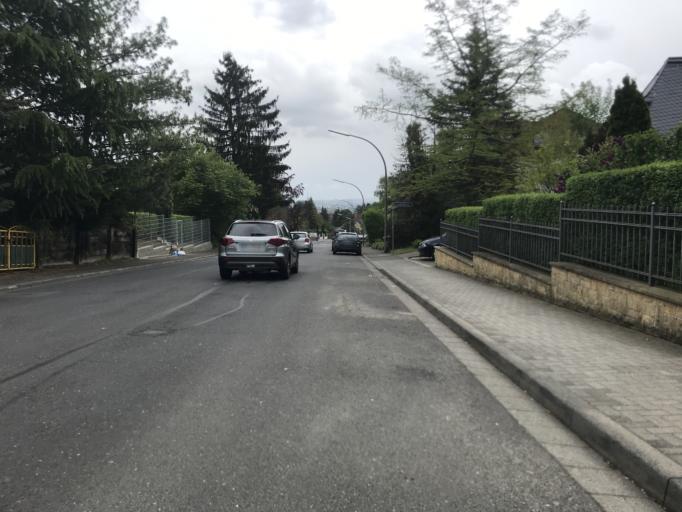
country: DE
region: Hesse
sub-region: Regierungsbezirk Darmstadt
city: Walluf
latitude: 50.0605
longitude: 8.1890
